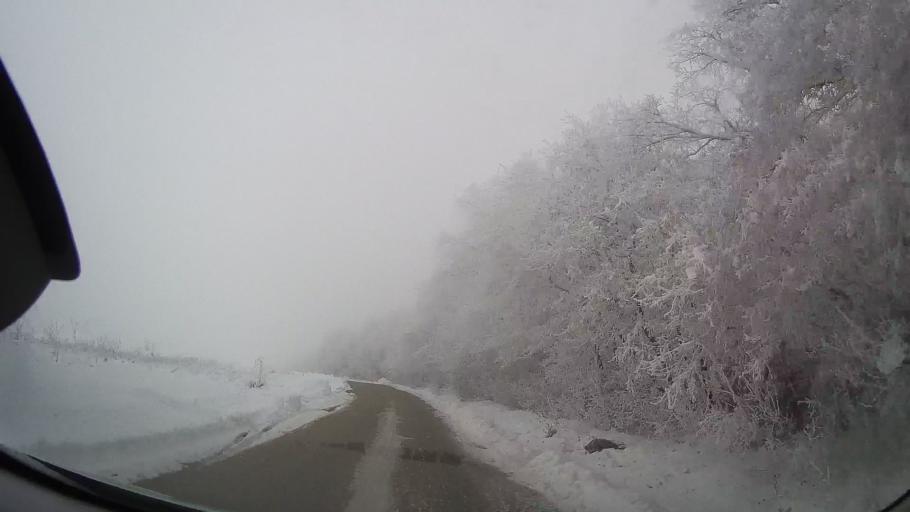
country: RO
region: Iasi
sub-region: Comuna Dagata
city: Dagata
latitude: 46.9189
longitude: 27.1790
